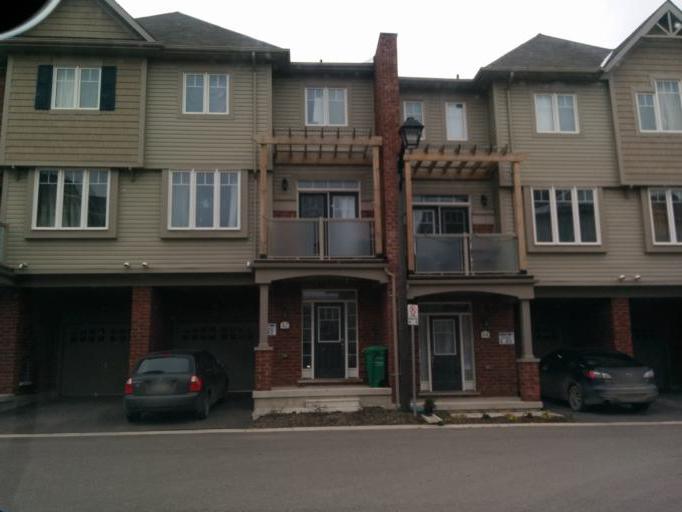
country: CA
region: Ontario
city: Brampton
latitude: 43.7546
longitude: -79.8256
